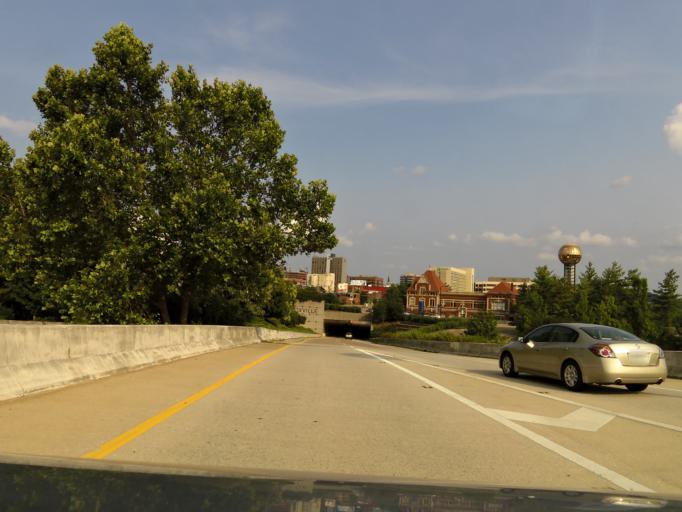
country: US
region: Tennessee
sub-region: Knox County
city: Knoxville
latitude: 35.9659
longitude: -83.9261
